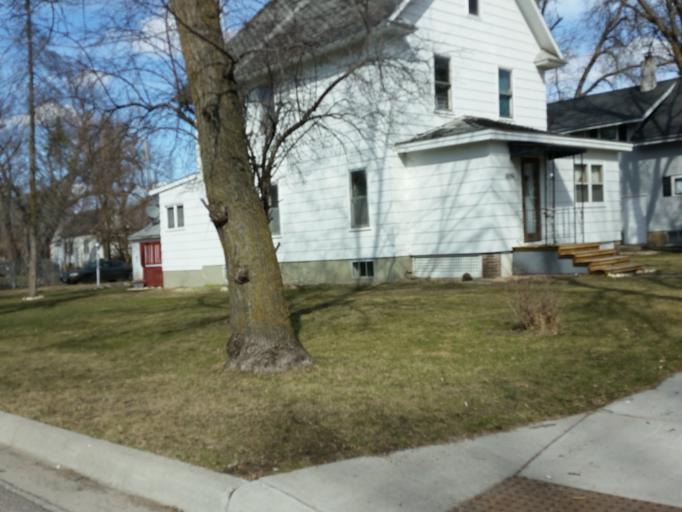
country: US
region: Minnesota
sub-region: Lac qui Parle County
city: Dawson
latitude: 44.9310
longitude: -96.0616
